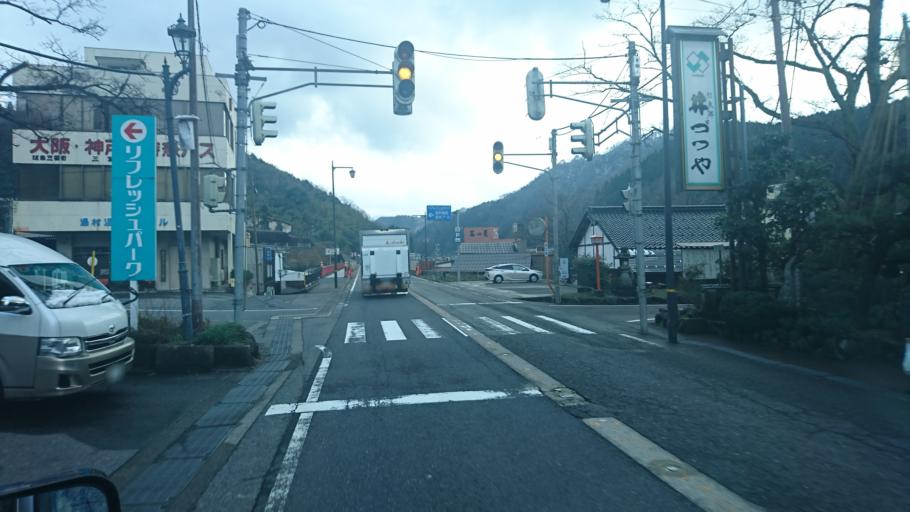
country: JP
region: Tottori
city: Tottori
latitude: 35.5561
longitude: 134.4895
